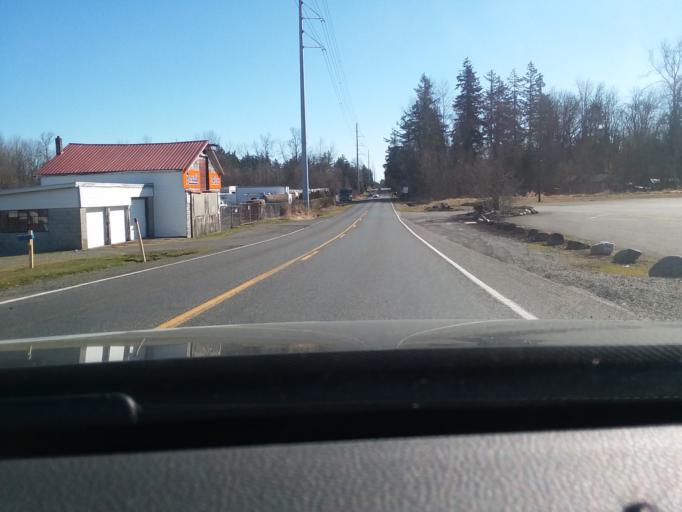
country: US
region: Washington
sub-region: Pierce County
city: Midland
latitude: 47.1808
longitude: -122.3888
